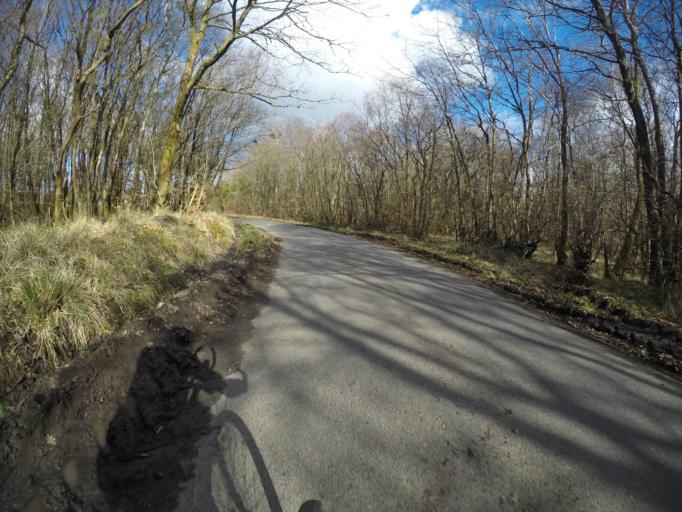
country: GB
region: Scotland
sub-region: North Ayrshire
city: Irvine
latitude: 55.6720
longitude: -4.6559
